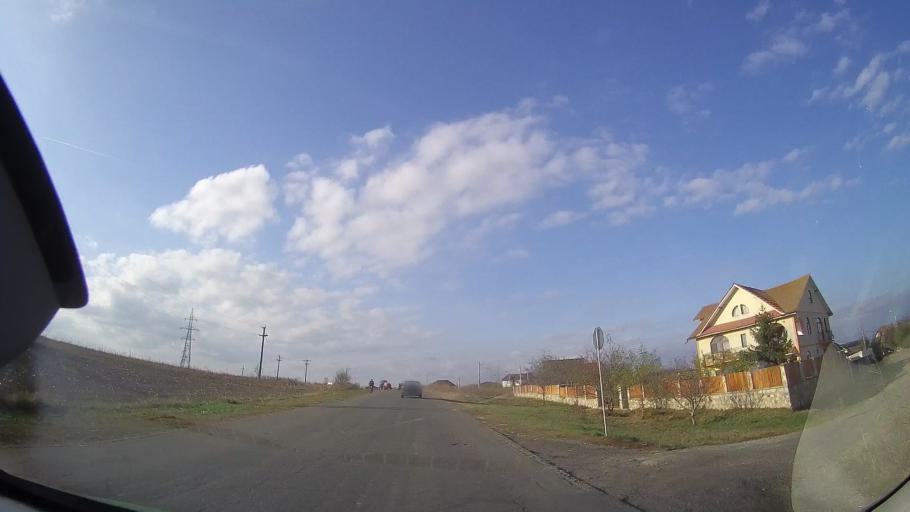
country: RO
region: Constanta
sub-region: Comuna Limanu
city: Limanu
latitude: 43.7927
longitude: 28.5453
